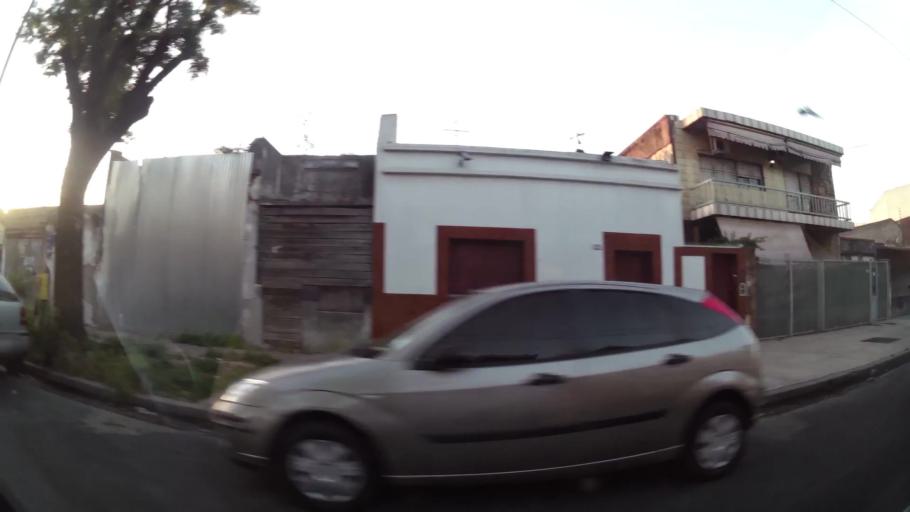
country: AR
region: Buenos Aires F.D.
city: Villa Lugano
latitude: -34.6710
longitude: -58.4729
